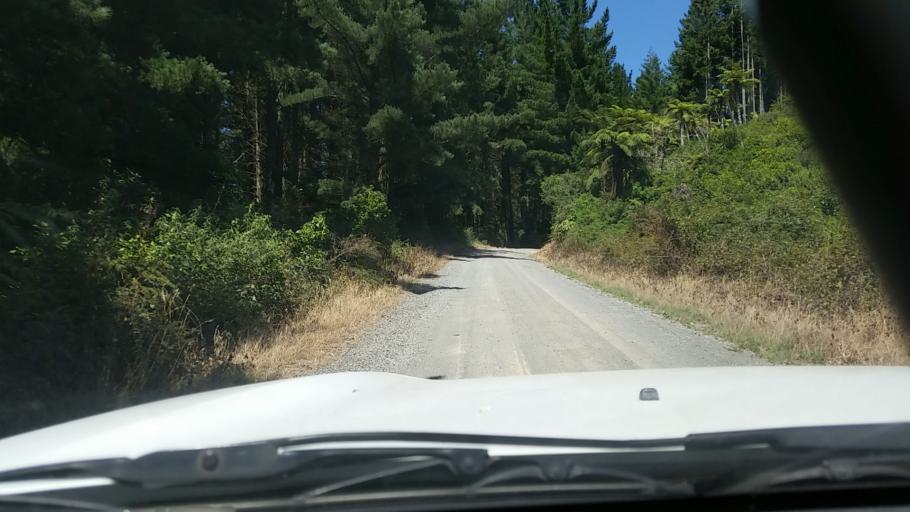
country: NZ
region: Bay of Plenty
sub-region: Whakatane District
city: Murupara
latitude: -38.3471
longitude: 176.5438
